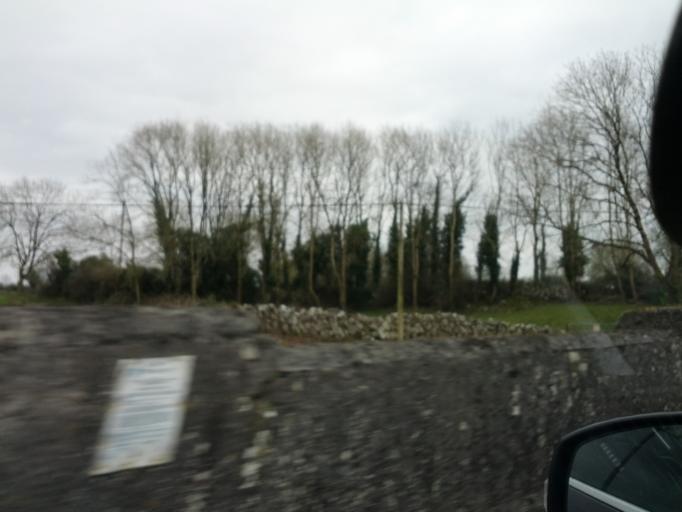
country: IE
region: Connaught
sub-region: County Galway
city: Athenry
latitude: 53.2135
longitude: -8.8168
